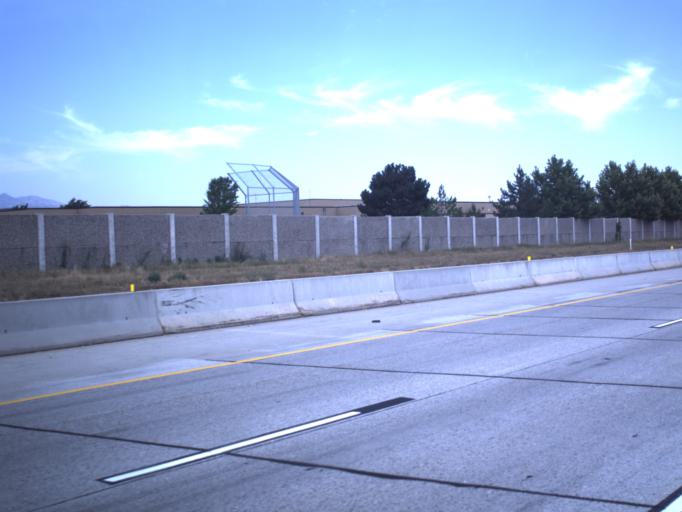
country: US
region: Utah
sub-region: Salt Lake County
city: South Jordan Heights
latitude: 40.5704
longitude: -111.9770
